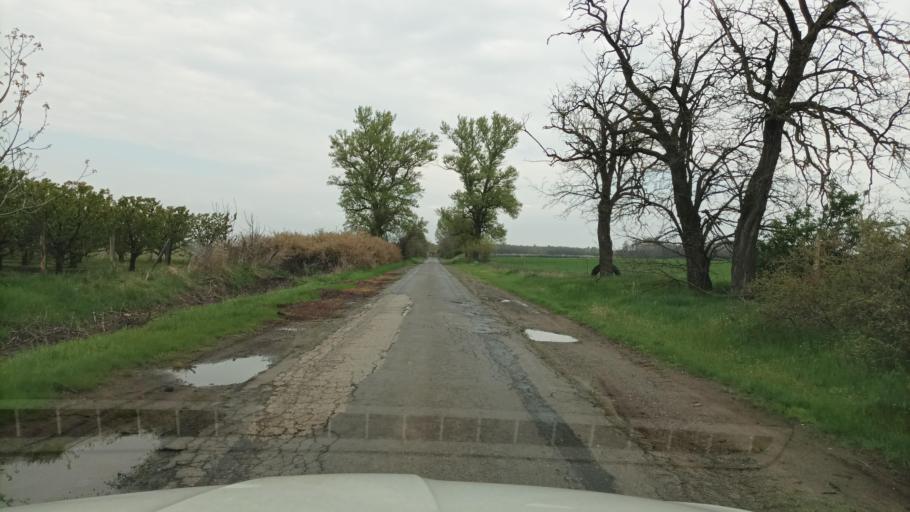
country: HU
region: Pest
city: Nagykoros
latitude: 46.9961
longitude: 19.8012
